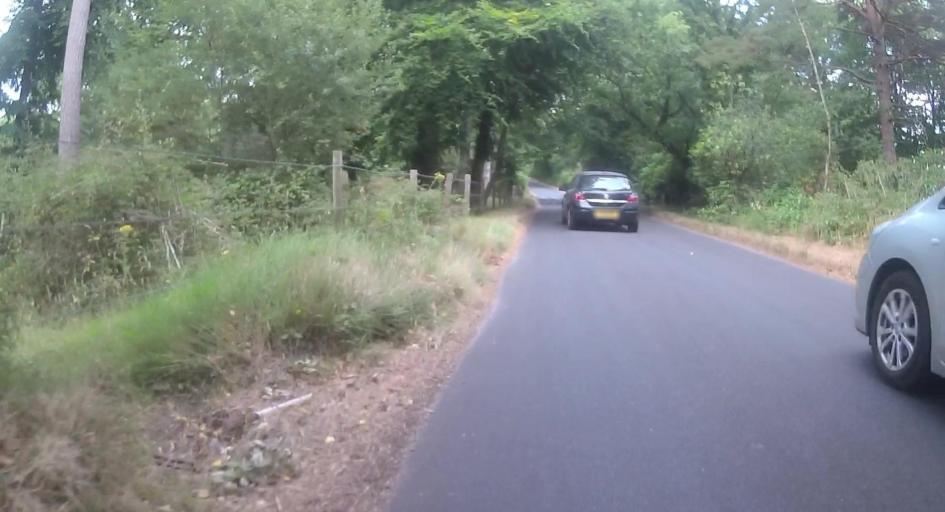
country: GB
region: England
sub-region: Dorset
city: Wareham
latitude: 50.6689
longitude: -2.1278
